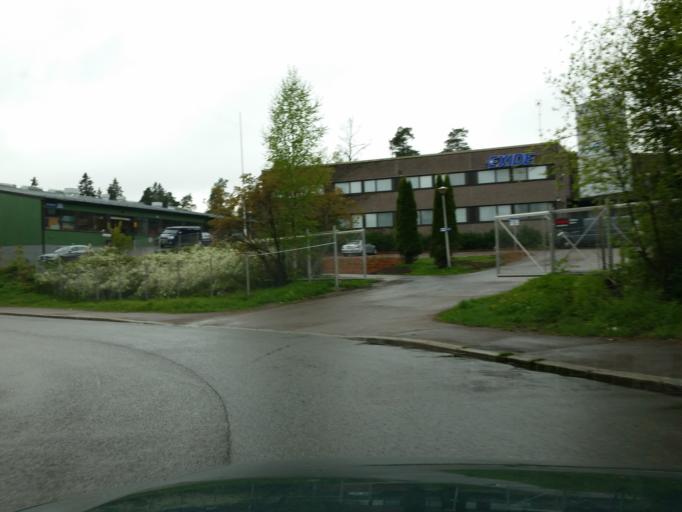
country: FI
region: Uusimaa
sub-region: Helsinki
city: Teekkarikylae
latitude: 60.2221
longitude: 24.8485
